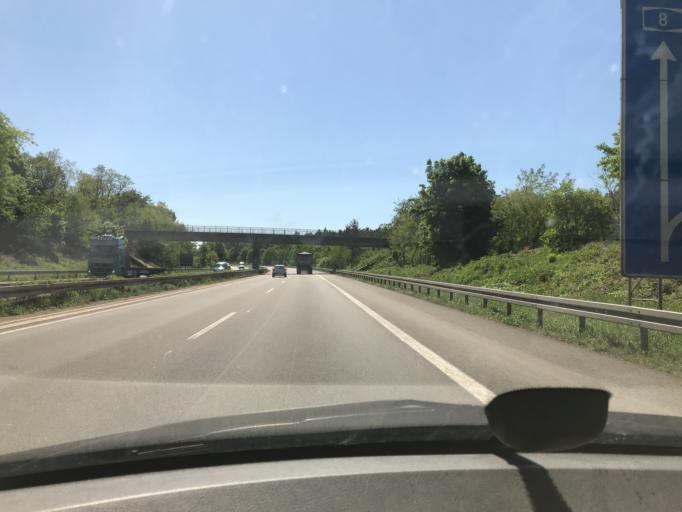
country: DE
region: Saarland
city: Saarwellingen
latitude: 49.3363
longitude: 6.8043
